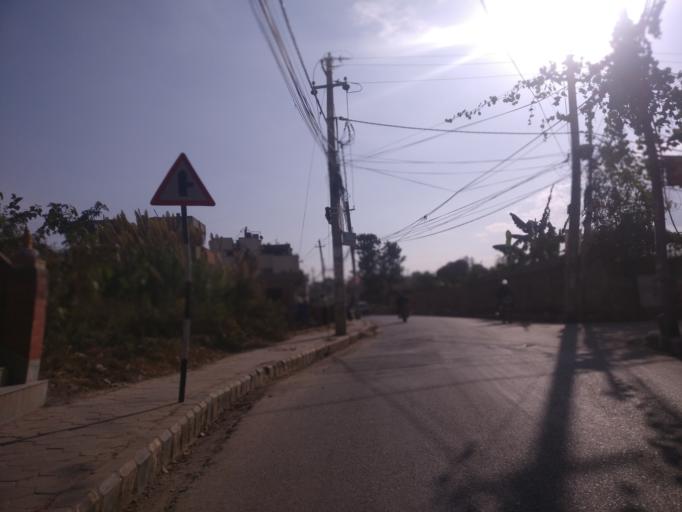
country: NP
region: Central Region
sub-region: Bagmati Zone
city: Patan
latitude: 27.6832
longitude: 85.3259
